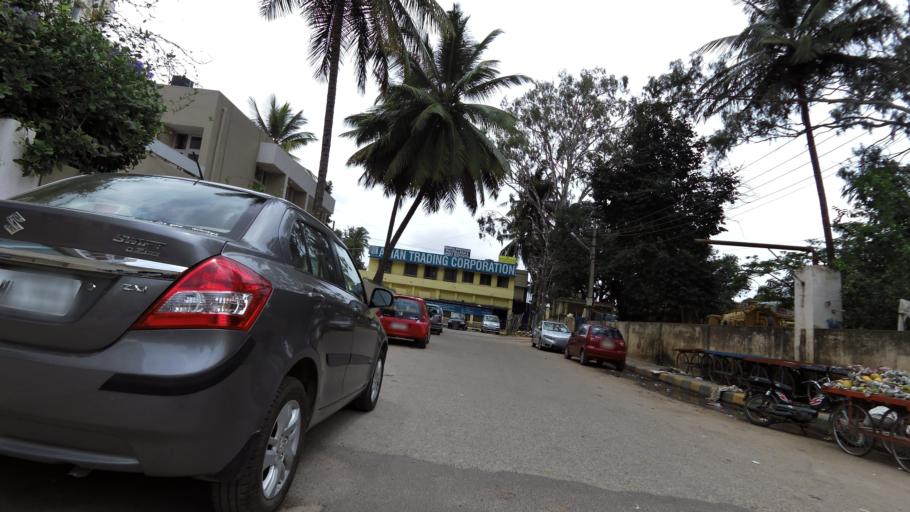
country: IN
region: Karnataka
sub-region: Bangalore Urban
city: Bangalore
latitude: 13.0012
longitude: 77.6272
